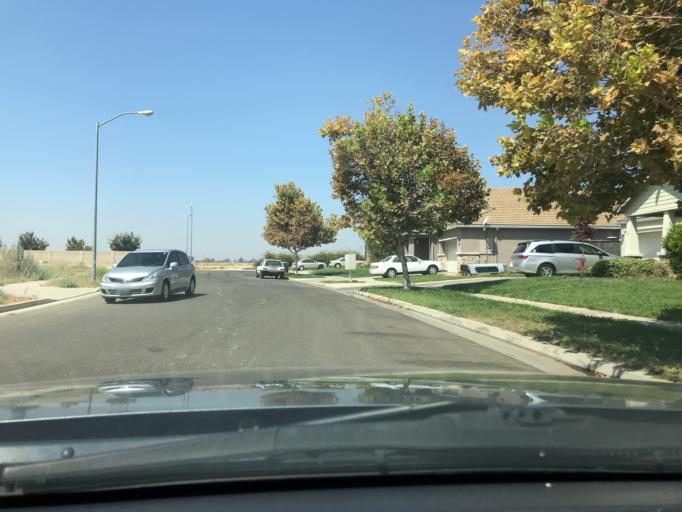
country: US
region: California
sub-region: Merced County
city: Merced
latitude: 37.3508
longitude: -120.4763
